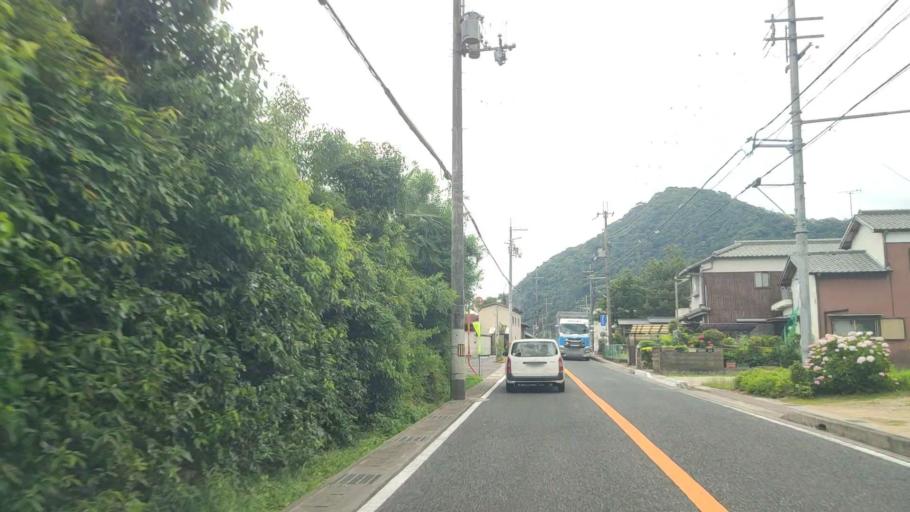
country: JP
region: Hyogo
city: Tatsunocho-tominaga
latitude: 34.8803
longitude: 134.5462
